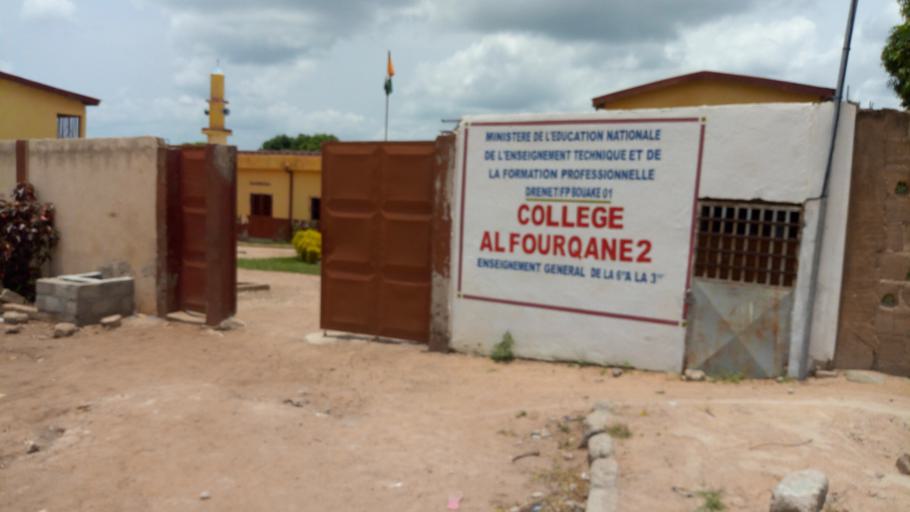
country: CI
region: Vallee du Bandama
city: Bouake
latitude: 7.6772
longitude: -5.0062
